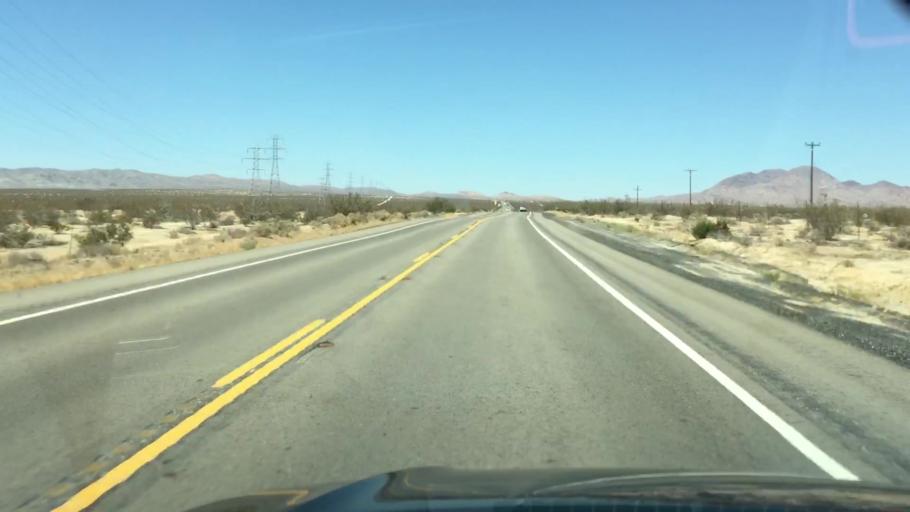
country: US
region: California
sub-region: Kern County
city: Boron
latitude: 35.2361
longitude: -117.6094
